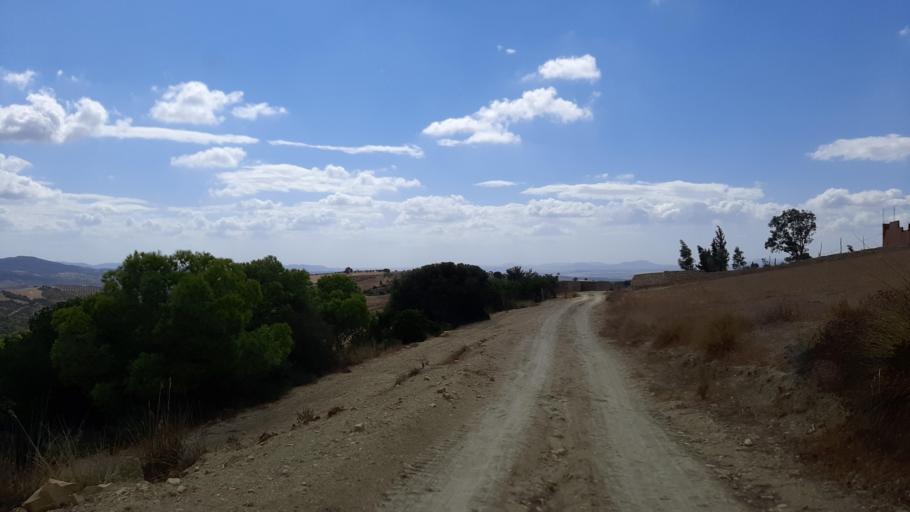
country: TN
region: Zaghwan
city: Zaghouan
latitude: 36.4915
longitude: 10.1766
